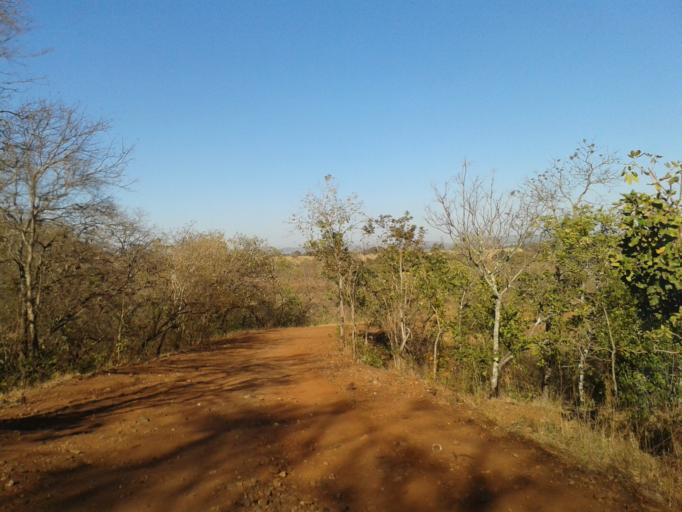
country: BR
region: Minas Gerais
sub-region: Santa Vitoria
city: Santa Vitoria
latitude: -18.9847
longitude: -49.8965
